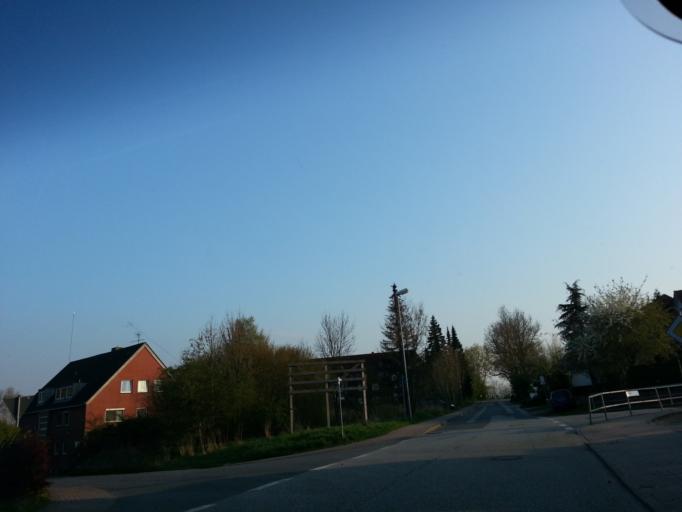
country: DE
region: Schleswig-Holstein
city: Timmendorfer Strand
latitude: 53.9891
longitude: 10.7681
